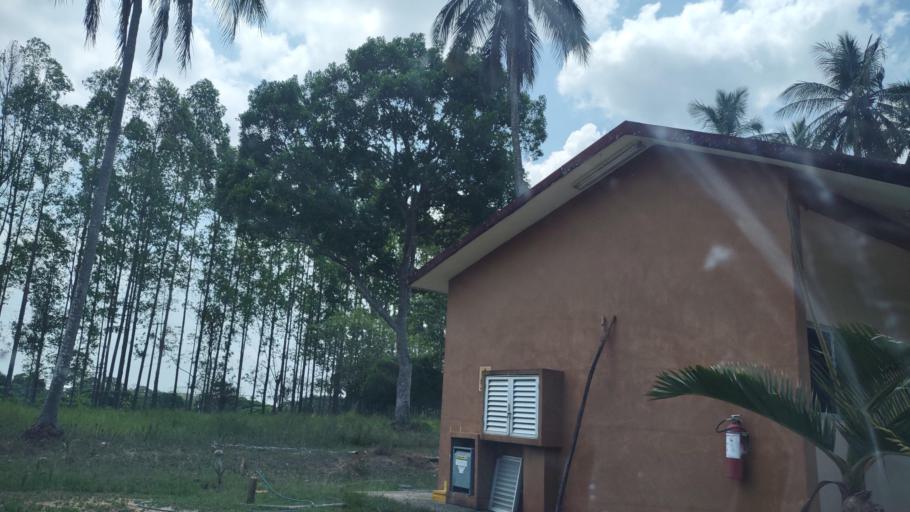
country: MX
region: Veracruz
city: Las Choapas
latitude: 17.9298
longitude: -94.1542
